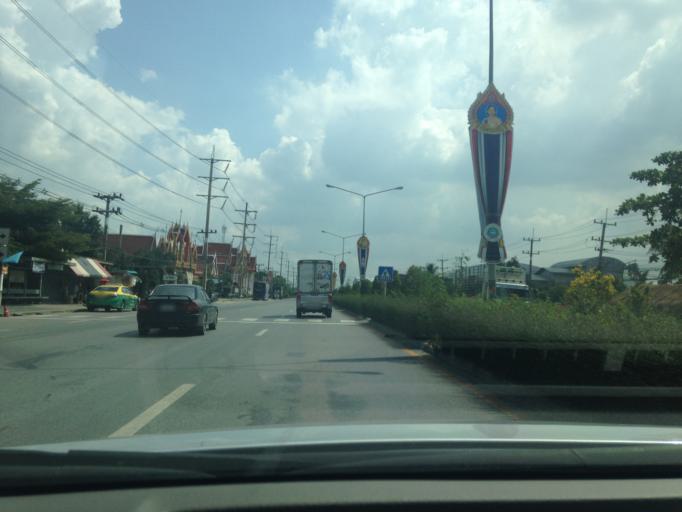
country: TH
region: Pathum Thani
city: Sam Khok
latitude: 14.0802
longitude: 100.5205
